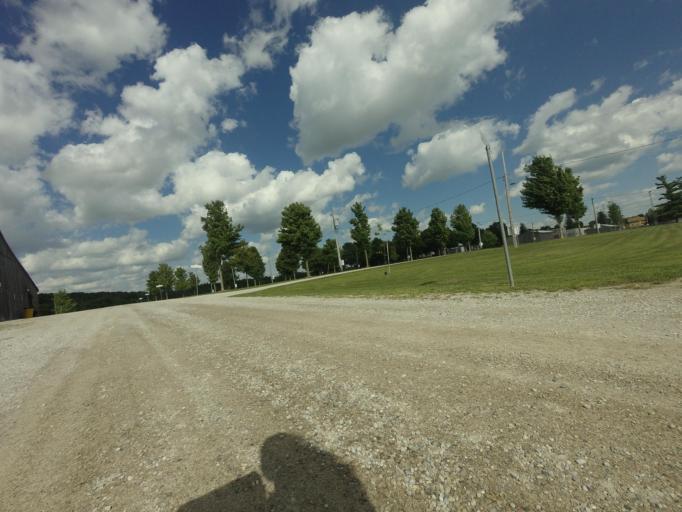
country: CA
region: Ontario
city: Huron East
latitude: 43.7371
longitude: -81.4358
